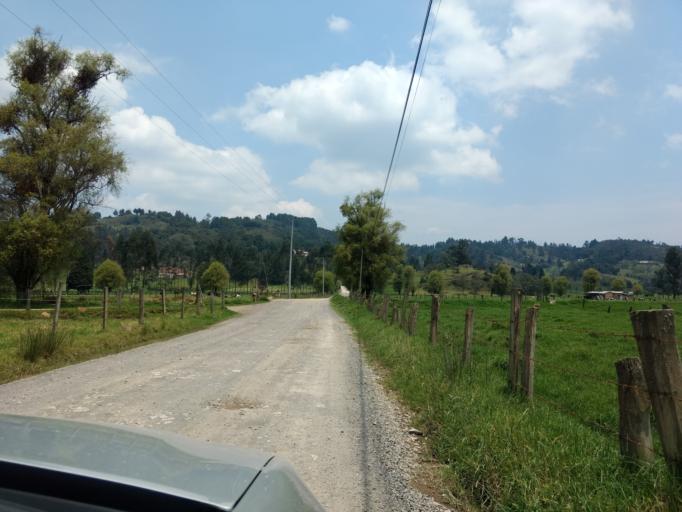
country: CO
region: Boyaca
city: Raquira
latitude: 5.5016
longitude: -73.7115
